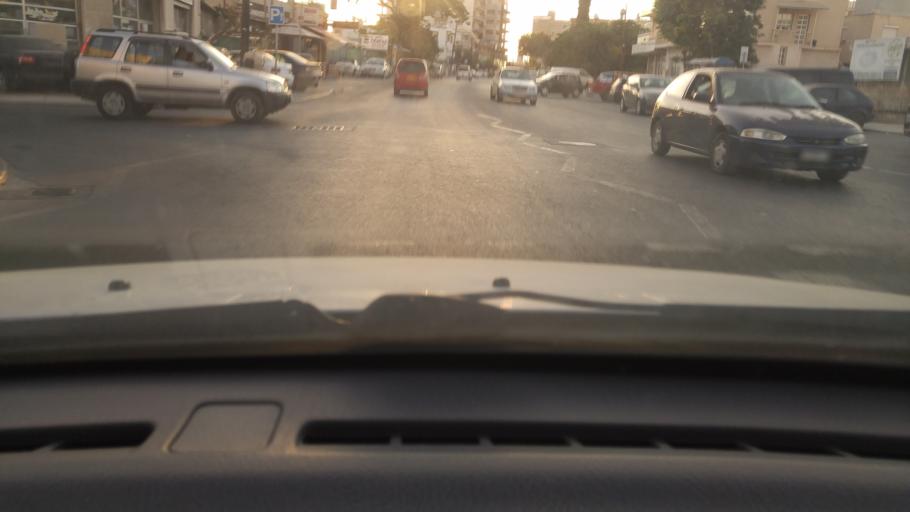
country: CY
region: Limassol
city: Limassol
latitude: 34.6735
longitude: 33.0204
